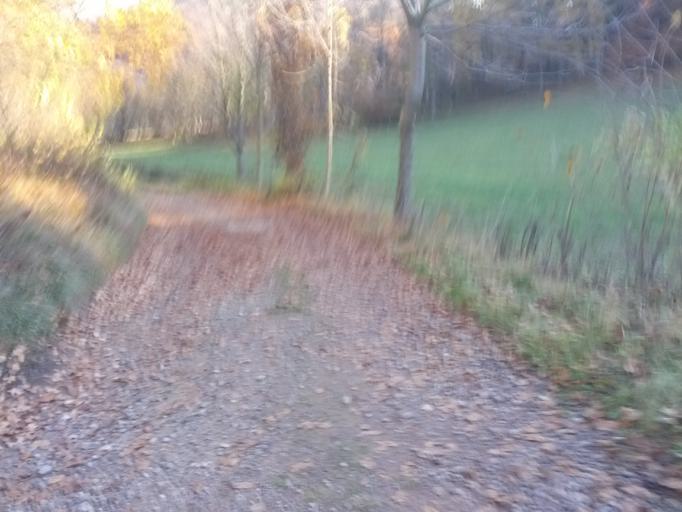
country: DE
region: Thuringia
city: Thal
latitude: 50.9263
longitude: 10.3928
